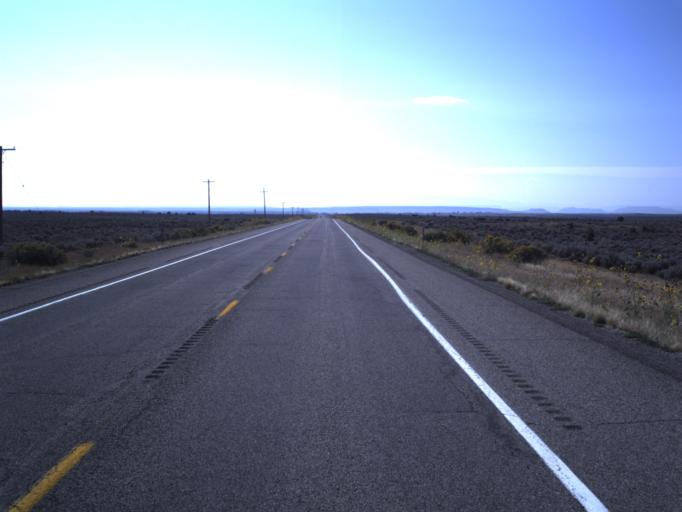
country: US
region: Utah
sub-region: San Juan County
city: Blanding
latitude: 37.5120
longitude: -109.4928
